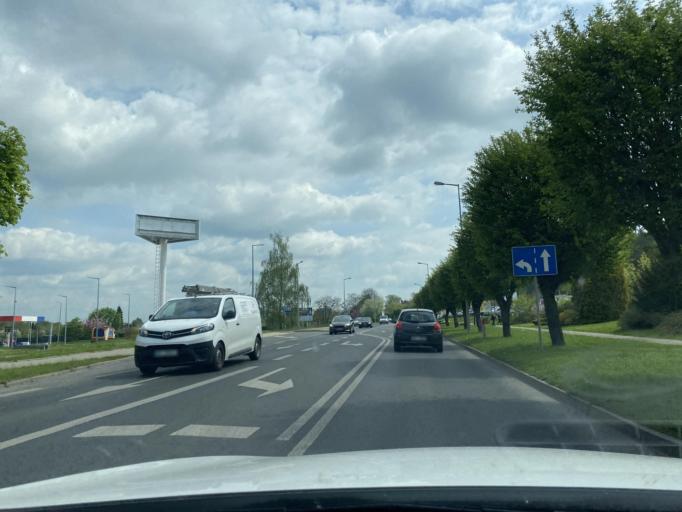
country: PL
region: Lower Silesian Voivodeship
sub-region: Powiat boleslawiecki
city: Boleslawiec
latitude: 51.2605
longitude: 15.5914
